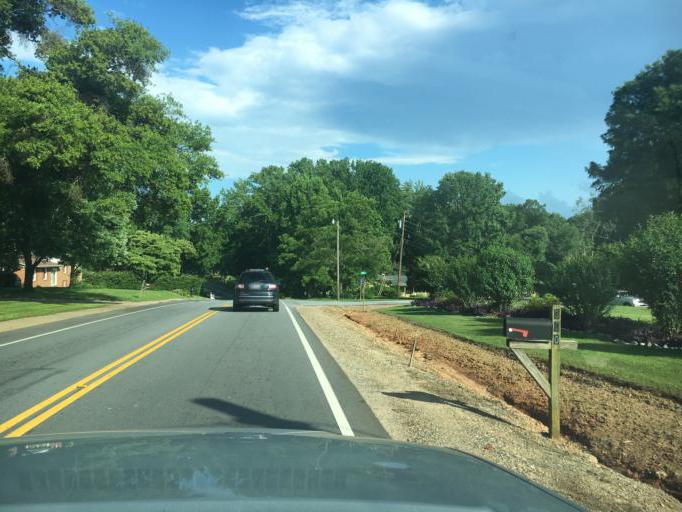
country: US
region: South Carolina
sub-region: Greenville County
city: Mauldin
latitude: 34.7816
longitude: -82.2918
